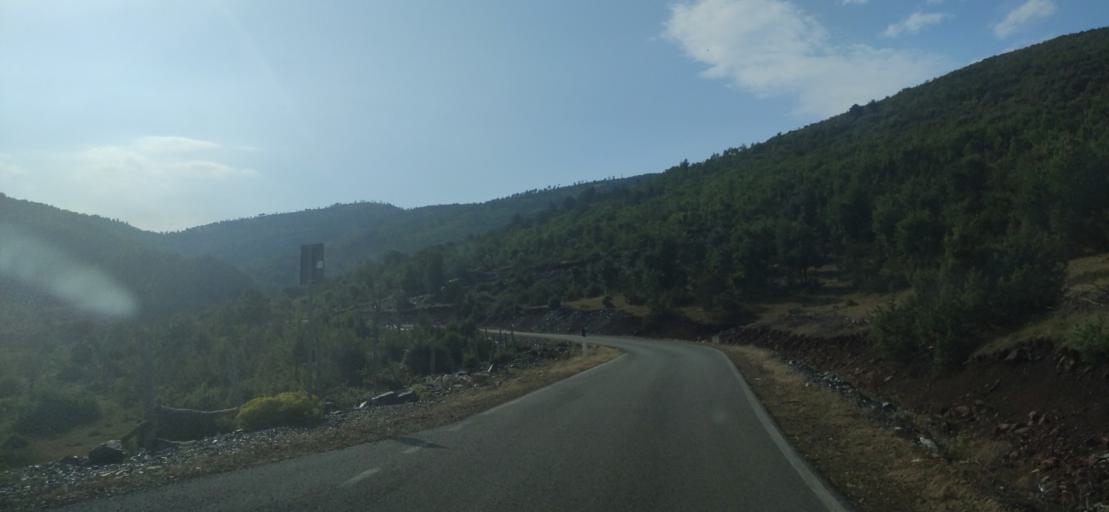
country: AL
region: Shkoder
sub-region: Rrethi i Pukes
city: Iballe
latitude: 42.1777
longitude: 20.0027
